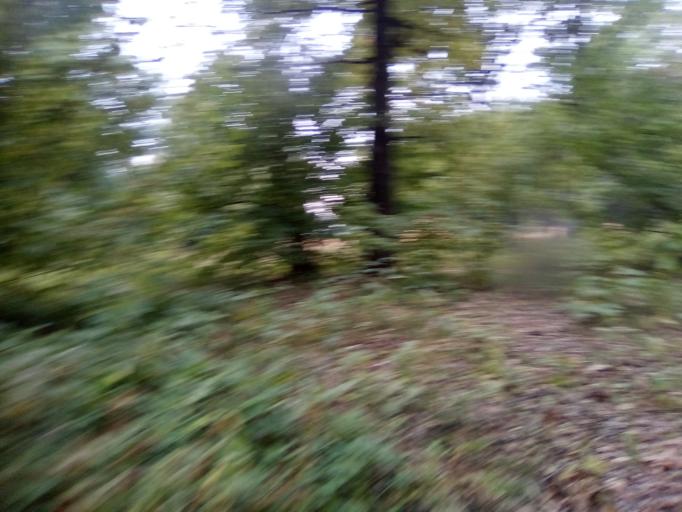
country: RU
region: Moskovskaya
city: Kokoshkino
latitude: 55.6132
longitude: 37.1885
